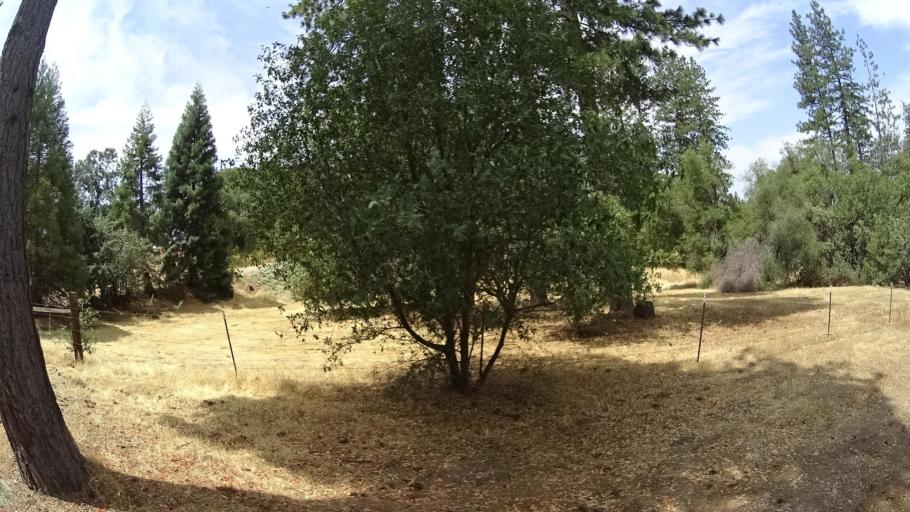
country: US
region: California
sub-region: Madera County
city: Ahwahnee
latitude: 37.4511
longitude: -119.8076
